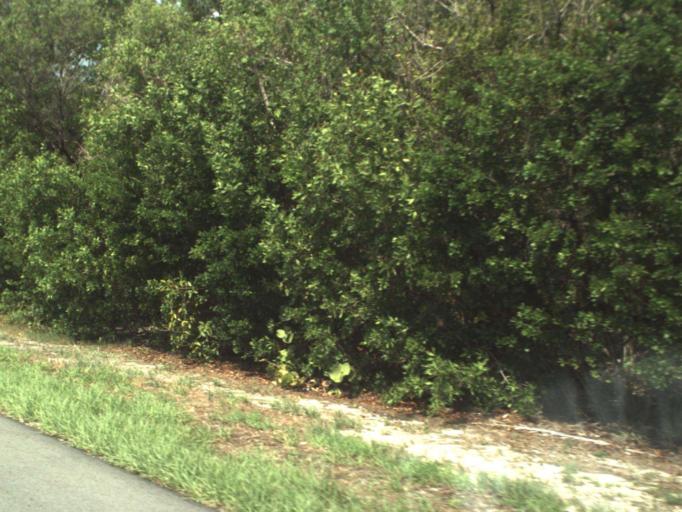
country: US
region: Florida
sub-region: Monroe County
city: Islamorada
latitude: 24.8306
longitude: -80.8078
